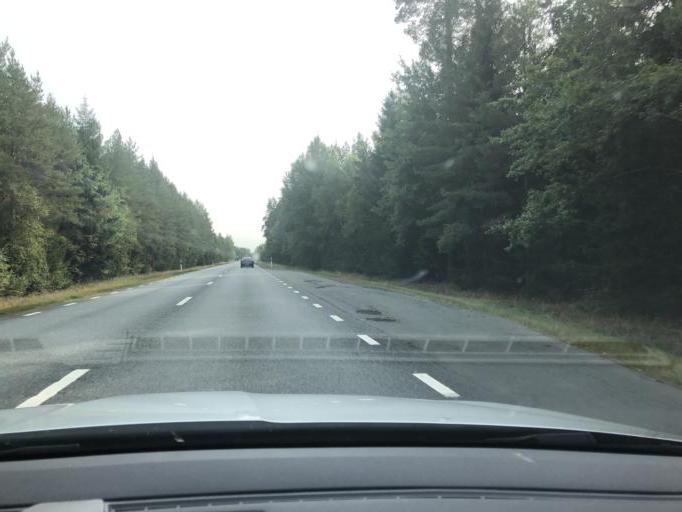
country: SE
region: Joenkoeping
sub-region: Eksjo Kommun
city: Eksjoe
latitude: 57.6237
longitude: 14.9694
